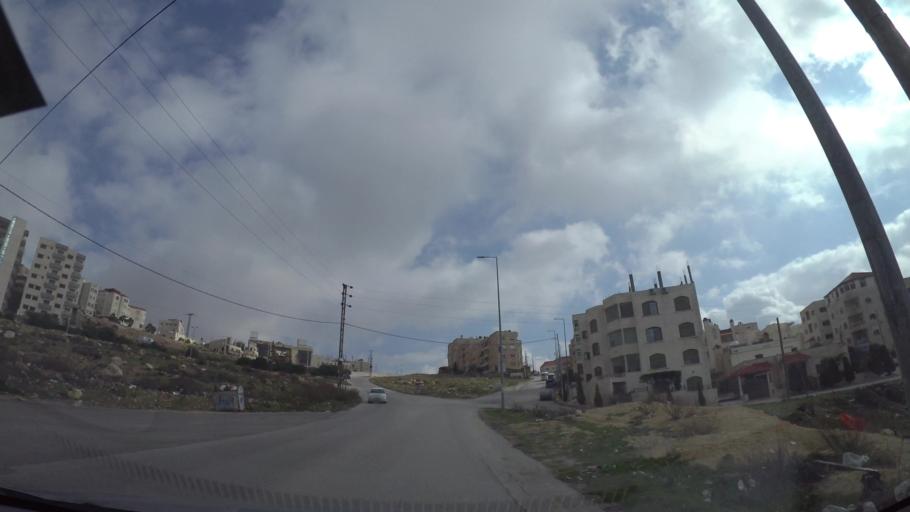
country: JO
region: Amman
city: Al Jubayhah
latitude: 32.0599
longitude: 35.8690
